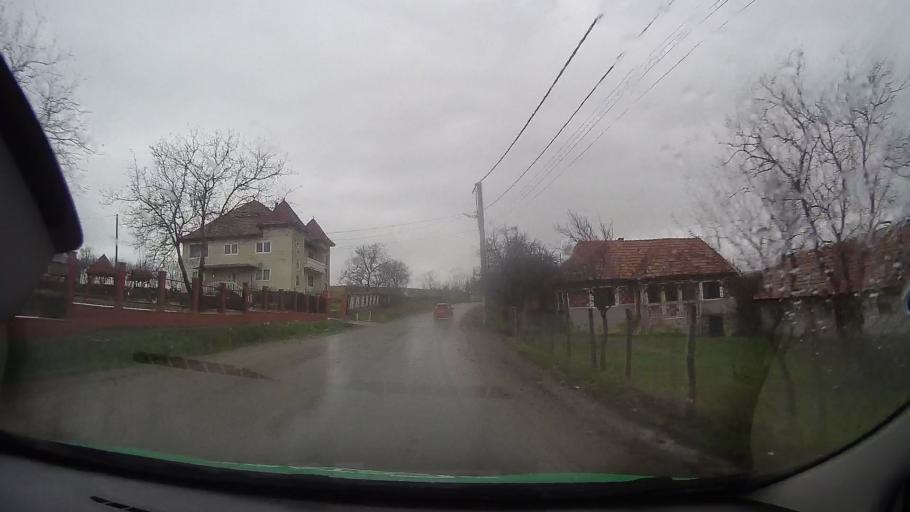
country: RO
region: Mures
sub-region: Comuna Vatava
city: Vatava
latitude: 46.9278
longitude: 24.7692
